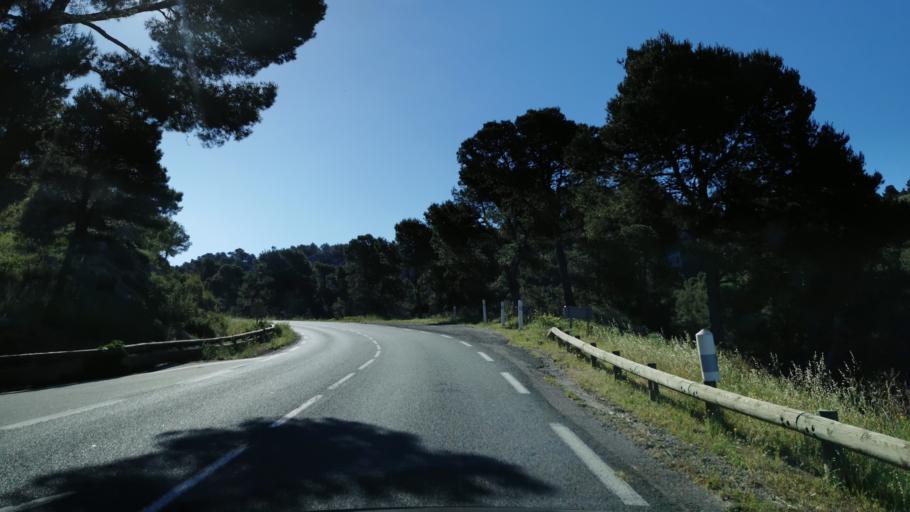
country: FR
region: Languedoc-Roussillon
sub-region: Departement de l'Aude
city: Armissan
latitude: 43.1747
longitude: 3.0845
